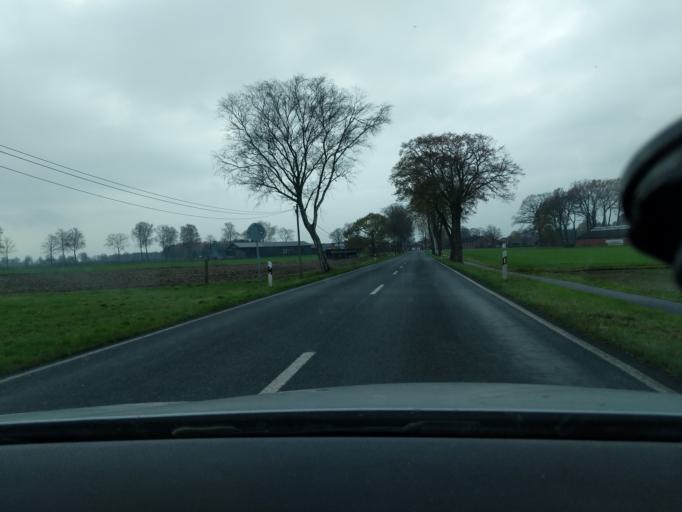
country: DE
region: Lower Saxony
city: Ahlerstedt
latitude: 53.3835
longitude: 9.4736
